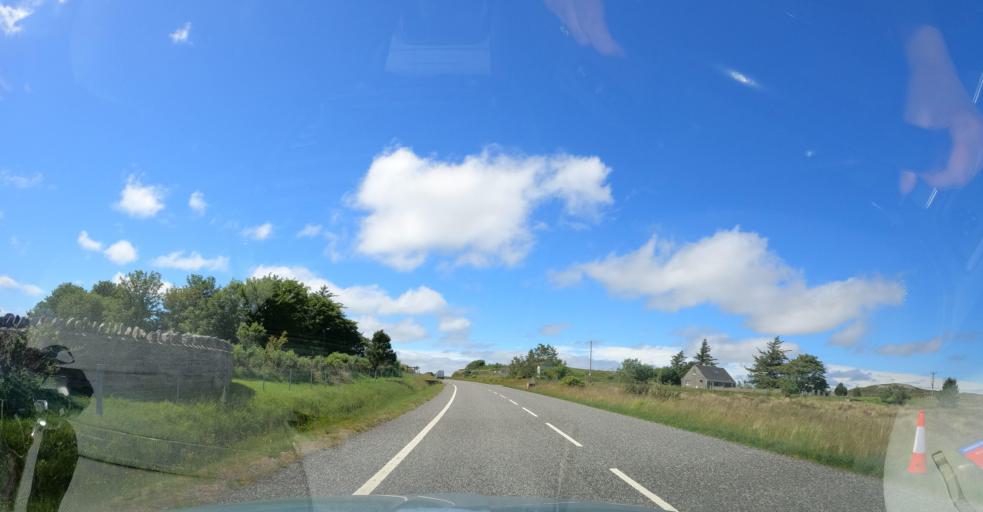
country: GB
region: Scotland
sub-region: Eilean Siar
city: Harris
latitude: 58.1924
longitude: -6.7103
